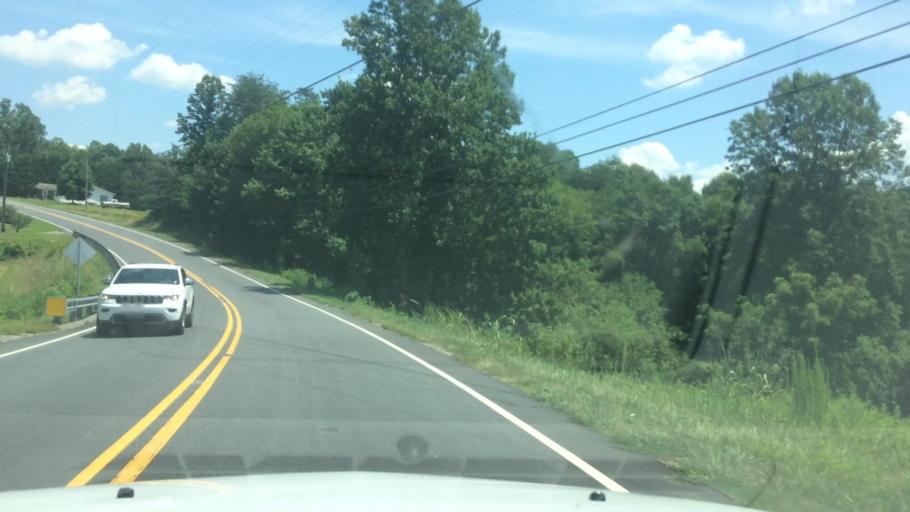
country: US
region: North Carolina
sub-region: Alexander County
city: Taylorsville
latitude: 35.9191
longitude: -81.2470
